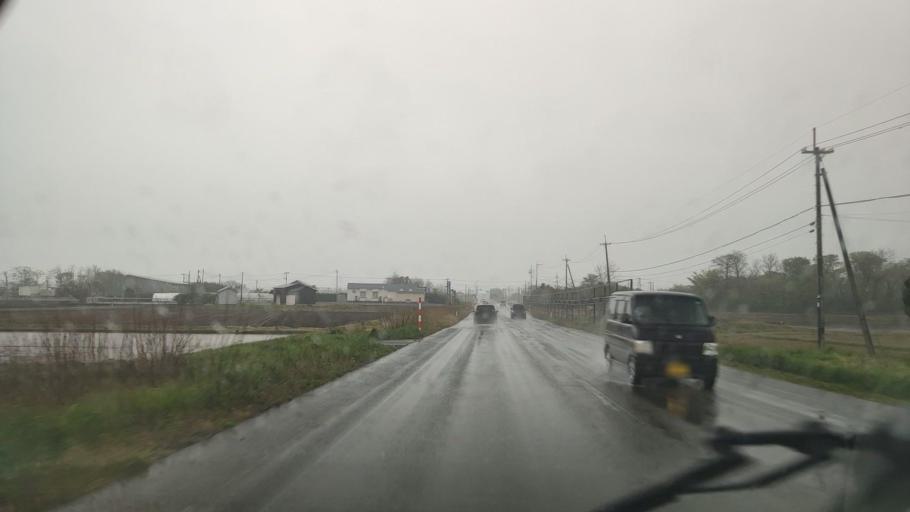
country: JP
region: Akita
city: Tenno
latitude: 39.9130
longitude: 139.9295
